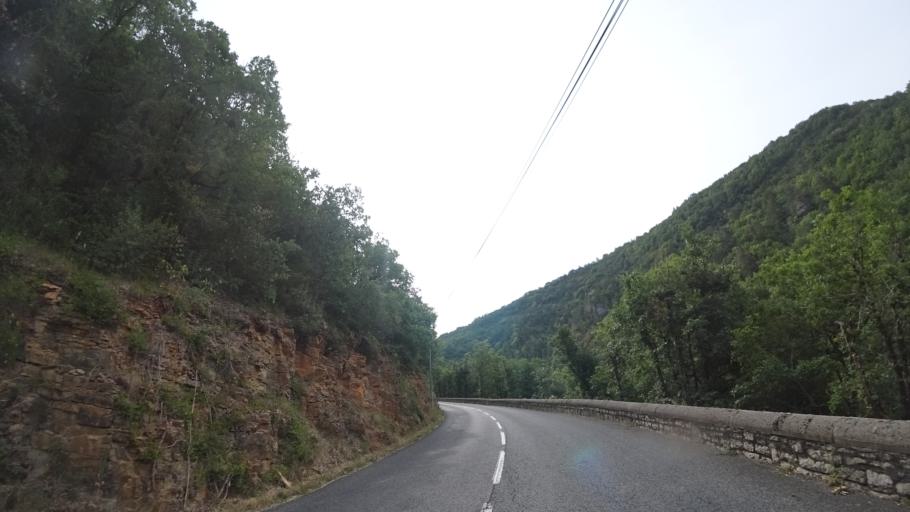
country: FR
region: Languedoc-Roussillon
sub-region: Departement de la Lozere
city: La Canourgue
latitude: 44.4084
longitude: 3.2448
